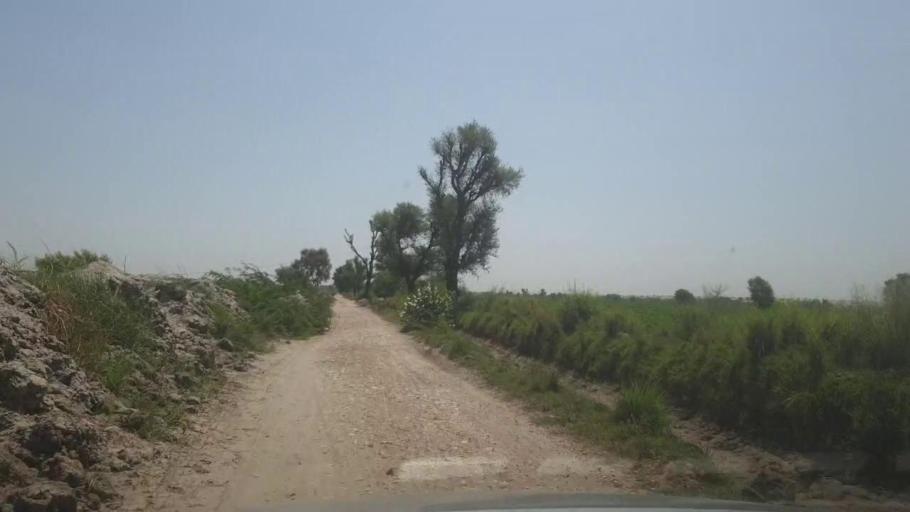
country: PK
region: Sindh
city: Khairpur
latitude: 27.3516
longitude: 69.0489
